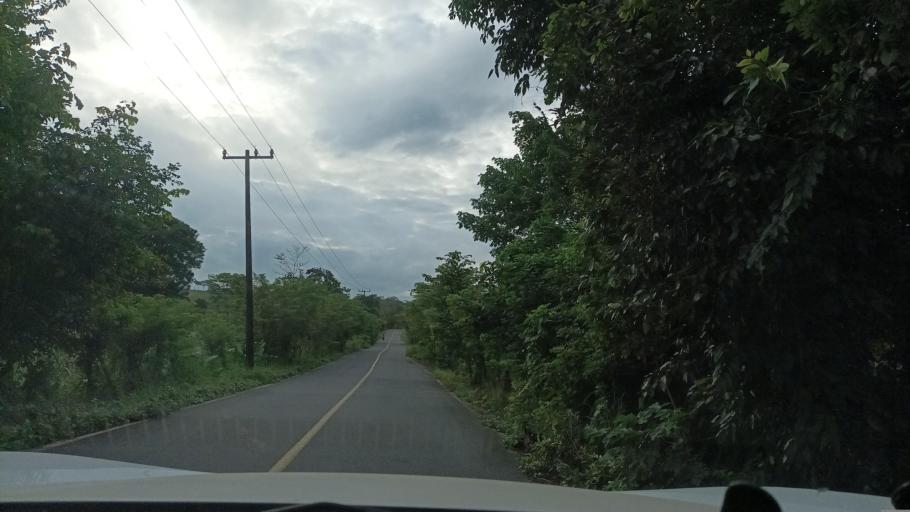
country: MX
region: Veracruz
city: Hidalgotitlan
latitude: 17.7128
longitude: -94.4710
